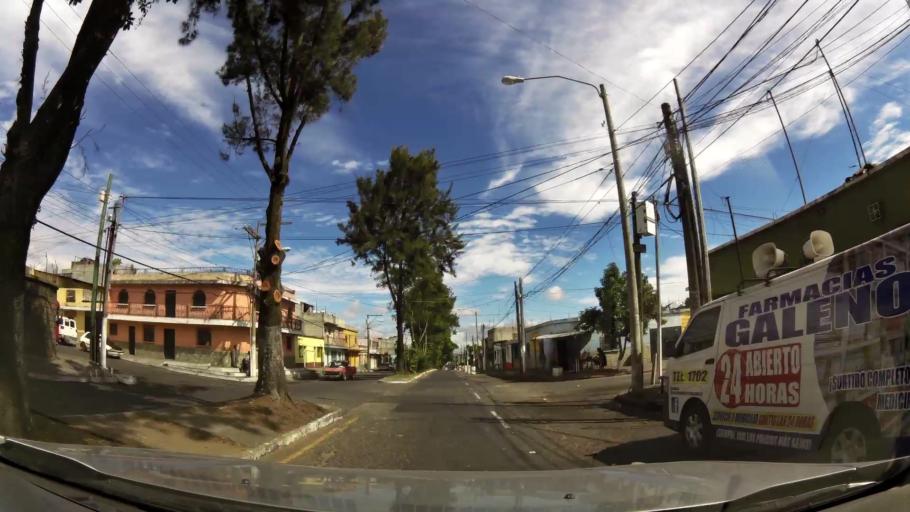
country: GT
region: Guatemala
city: Mixco
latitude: 14.6601
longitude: -90.5773
